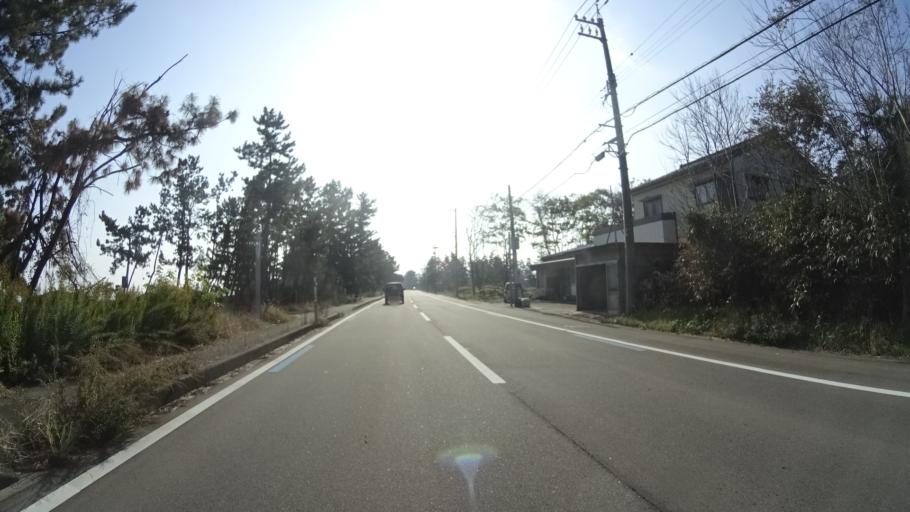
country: JP
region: Toyama
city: Himi
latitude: 36.8404
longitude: 137.0019
